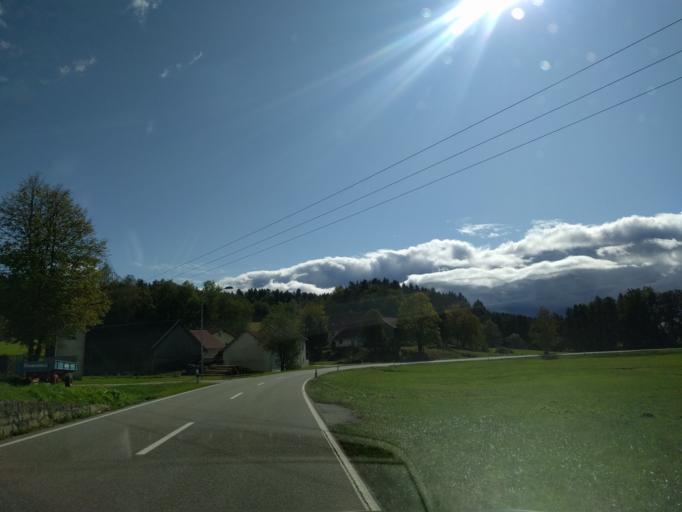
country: DE
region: Bavaria
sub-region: Lower Bavaria
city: Hengersberg
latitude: 48.8000
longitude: 13.0504
